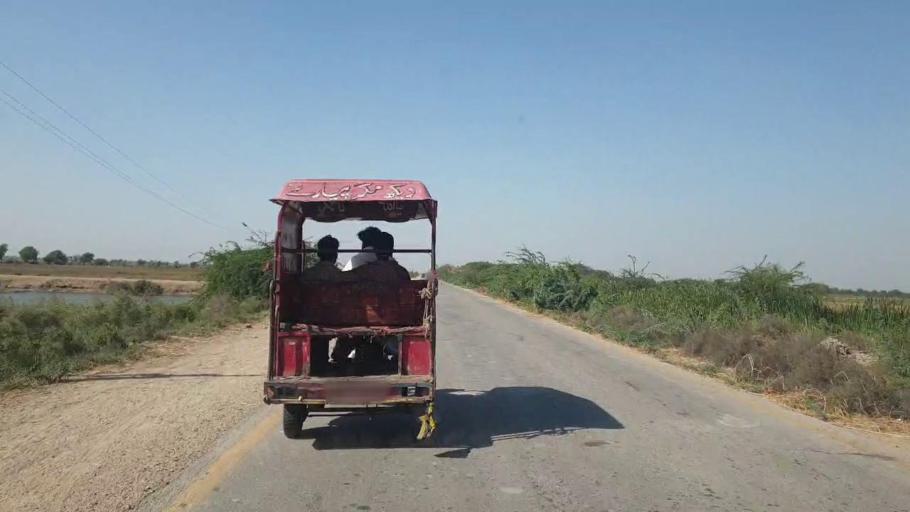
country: PK
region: Sindh
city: Rajo Khanani
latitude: 25.0473
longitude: 68.8103
